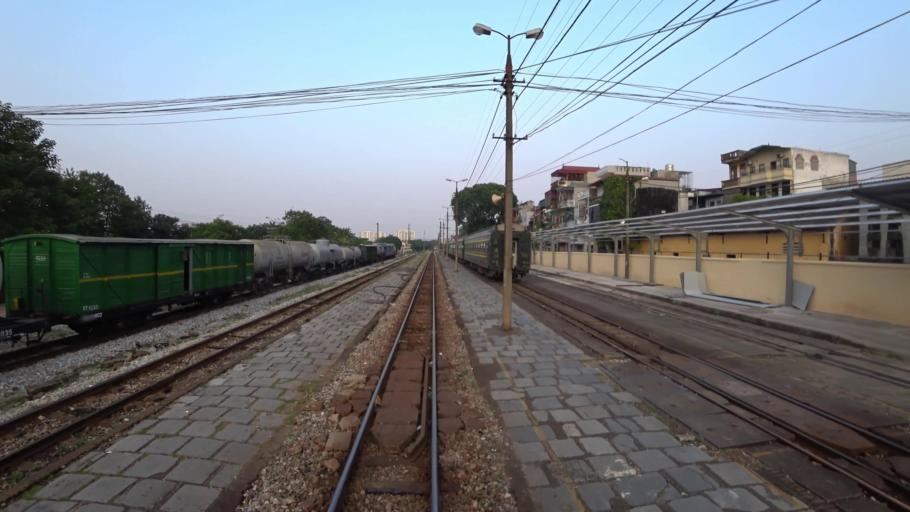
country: VN
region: Ha Noi
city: Hoan Kiem
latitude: 21.0642
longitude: 105.8955
